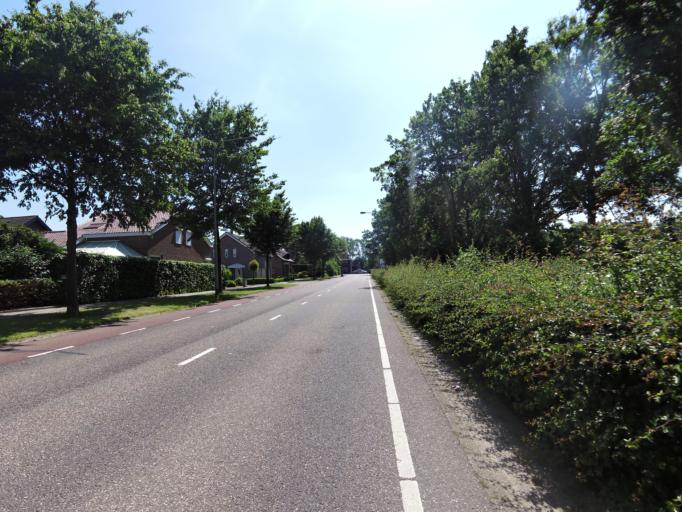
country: NL
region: Limburg
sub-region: Gemeente Kerkrade
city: Kerkrade
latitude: 50.9134
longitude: 6.0366
